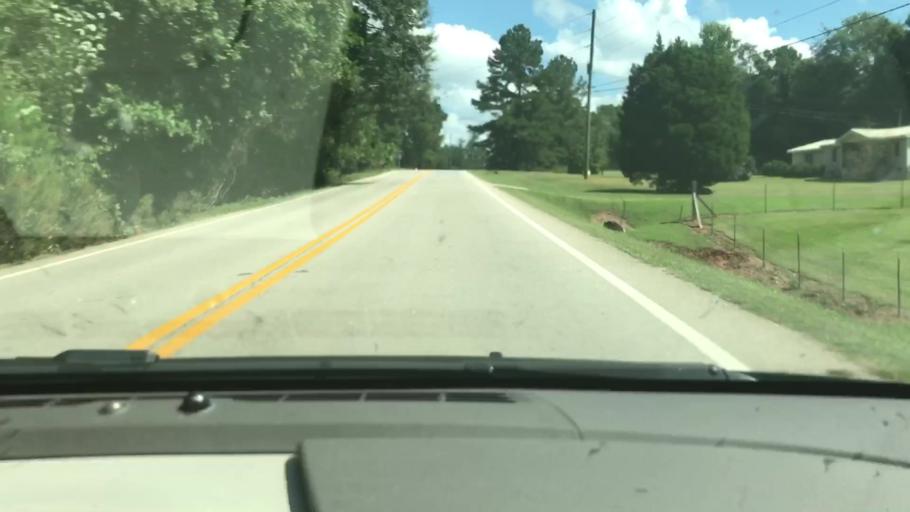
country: US
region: Georgia
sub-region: Troup County
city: La Grange
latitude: 32.8975
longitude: -85.0307
